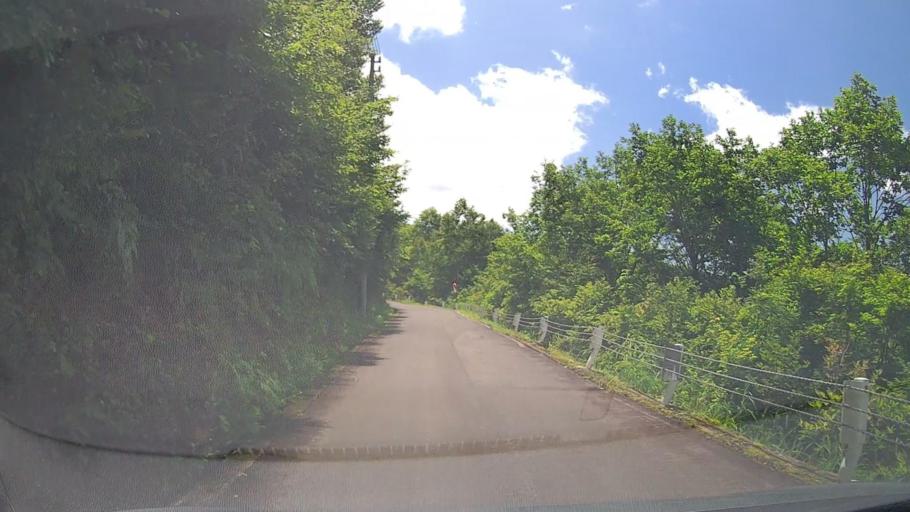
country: JP
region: Nagano
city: Iiyama
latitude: 36.9337
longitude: 138.4660
